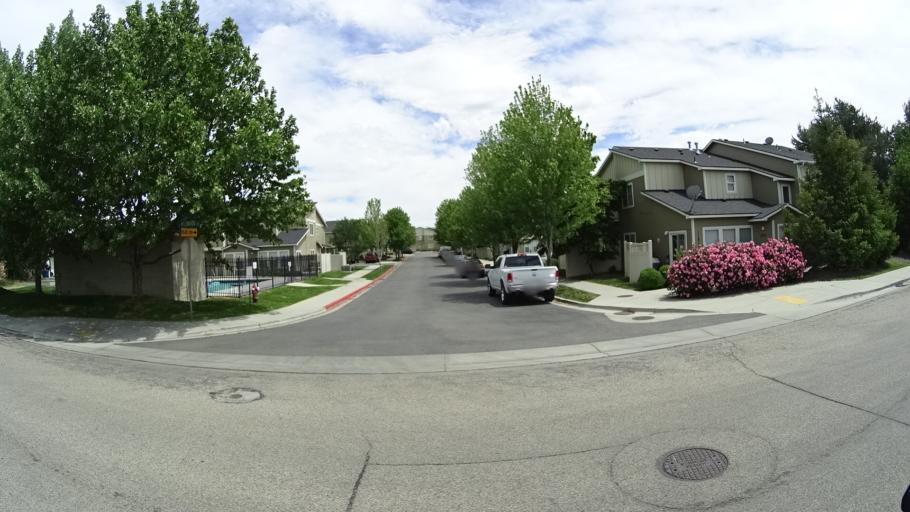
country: US
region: Idaho
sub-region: Ada County
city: Meridian
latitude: 43.6209
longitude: -116.3205
